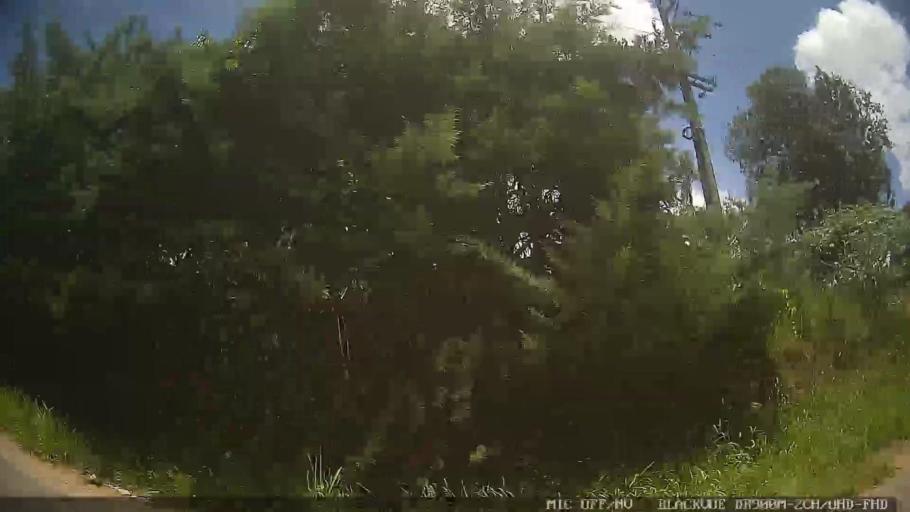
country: BR
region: Sao Paulo
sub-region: Braganca Paulista
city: Braganca Paulista
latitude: -22.9013
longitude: -46.5866
